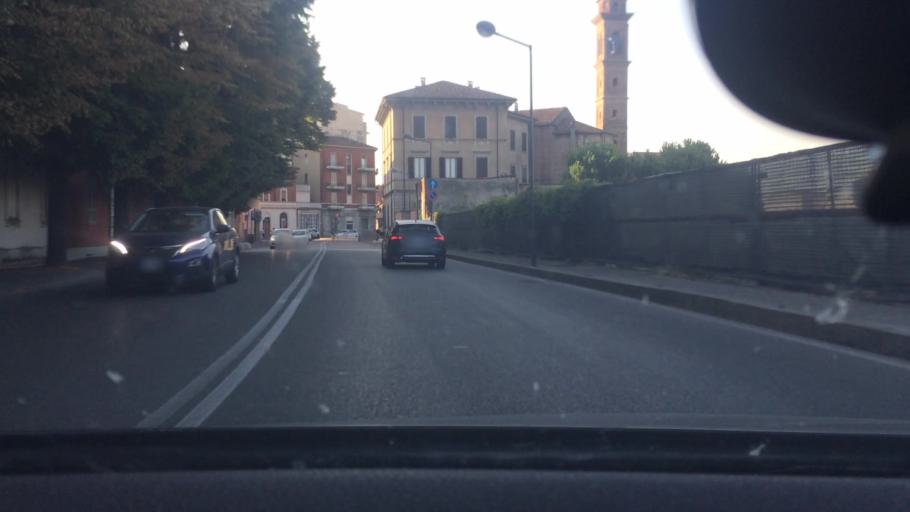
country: IT
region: Emilia-Romagna
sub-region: Provincia di Piacenza
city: Piacenza
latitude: 45.0488
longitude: 9.7067
